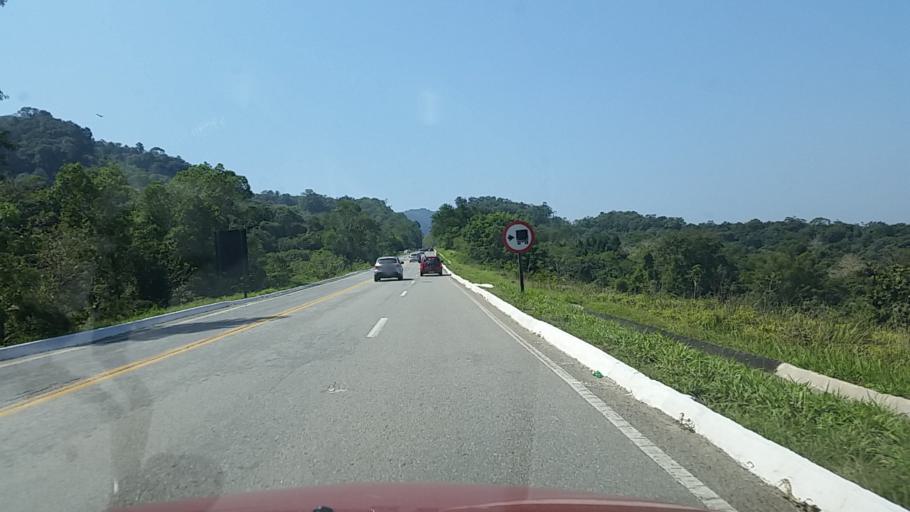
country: BR
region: Sao Paulo
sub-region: Miracatu
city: Miracatu
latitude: -24.3797
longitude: -47.5166
